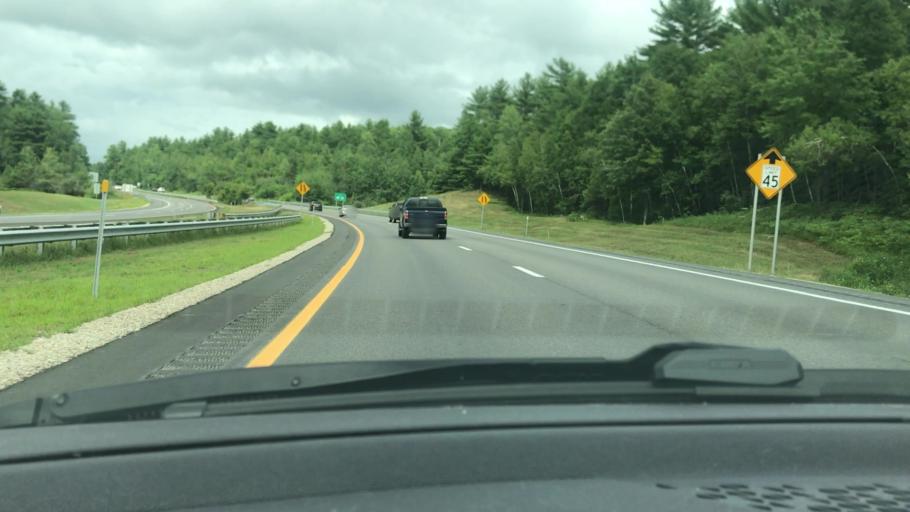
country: US
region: New Hampshire
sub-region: Merrimack County
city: Chichester
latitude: 43.2357
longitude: -71.4615
